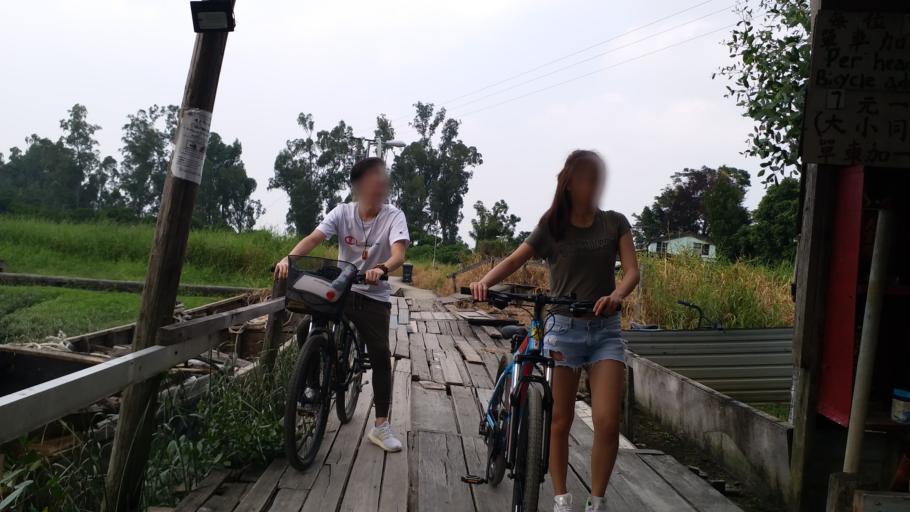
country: HK
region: Yuen Long
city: Yuen Long Kau Hui
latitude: 22.4543
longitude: 114.0349
